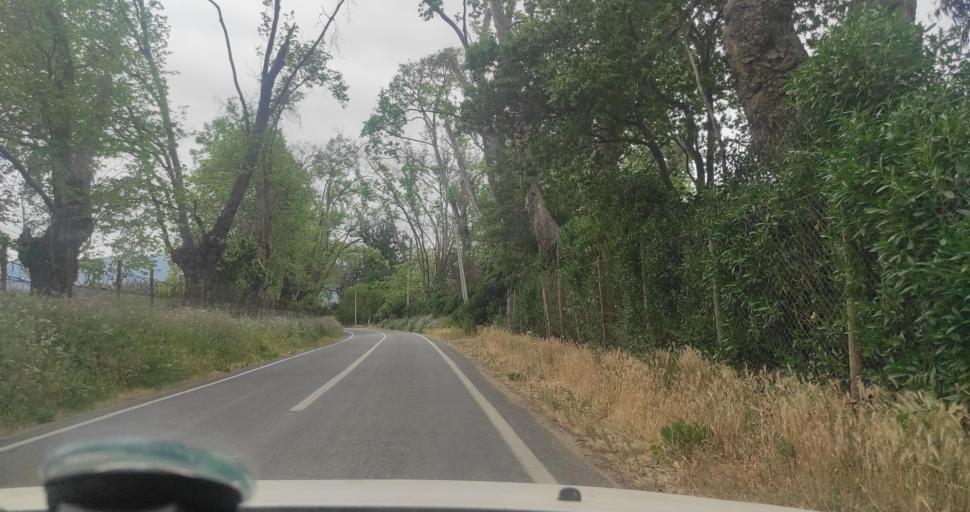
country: CL
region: Valparaiso
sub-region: Provincia de Marga Marga
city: Limache
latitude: -33.0288
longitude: -71.2395
